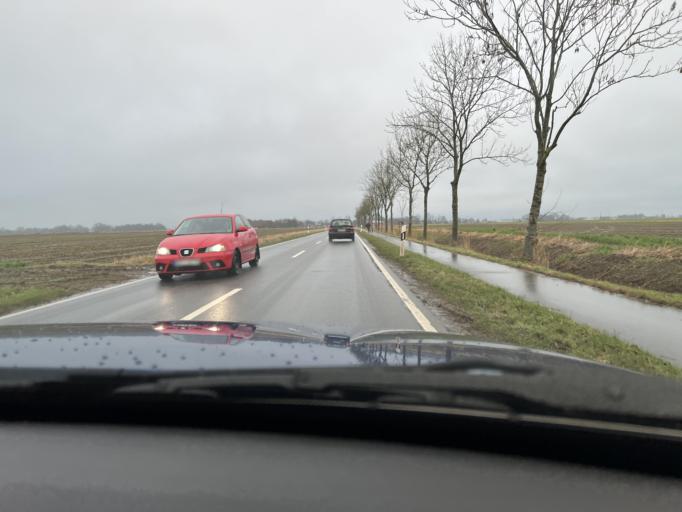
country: DE
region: Schleswig-Holstein
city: Wesselburen
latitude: 54.2065
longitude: 8.9419
